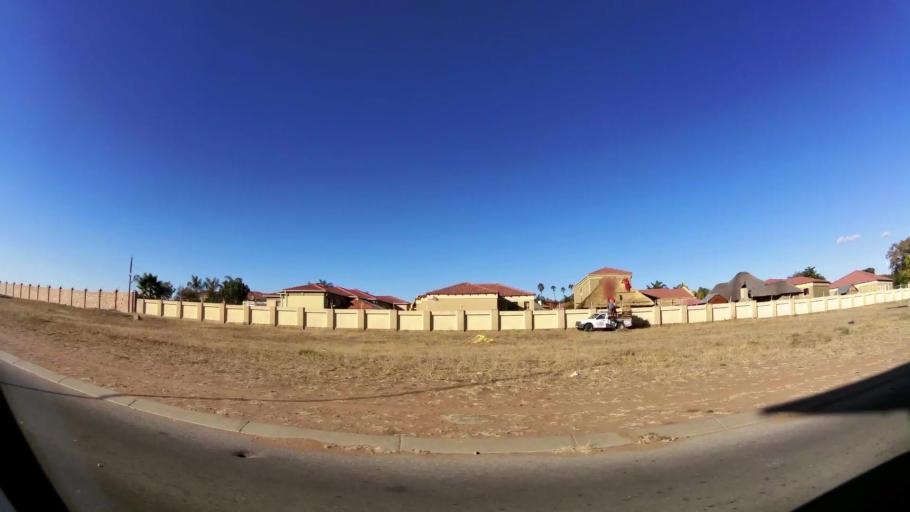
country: ZA
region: Limpopo
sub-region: Capricorn District Municipality
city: Polokwane
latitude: -23.8881
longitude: 29.4753
